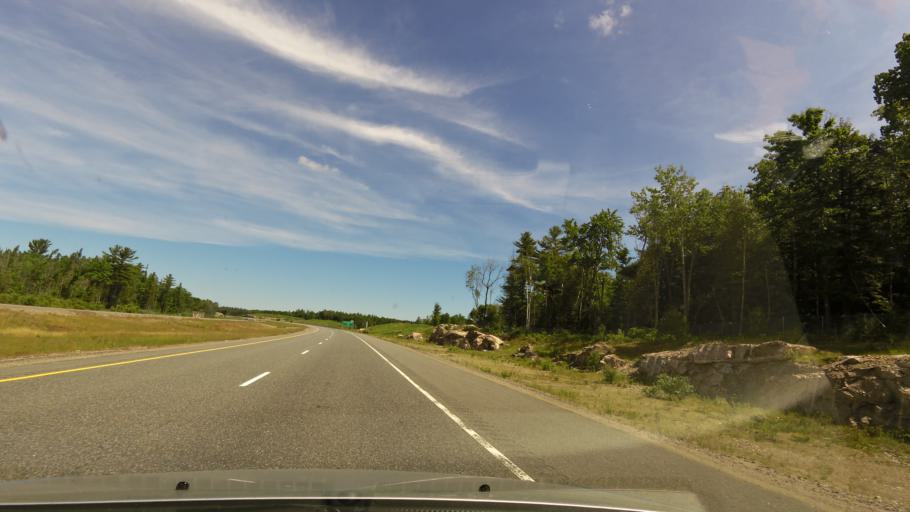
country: CA
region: Ontario
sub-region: Parry Sound District
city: Parry Sound
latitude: 45.4069
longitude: -80.0630
